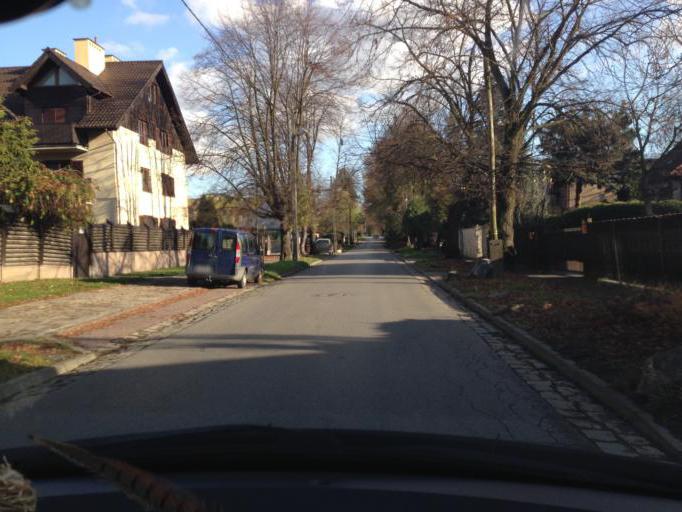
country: PL
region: Lesser Poland Voivodeship
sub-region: Powiat krakowski
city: Rzaska
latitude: 50.0673
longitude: 19.8521
